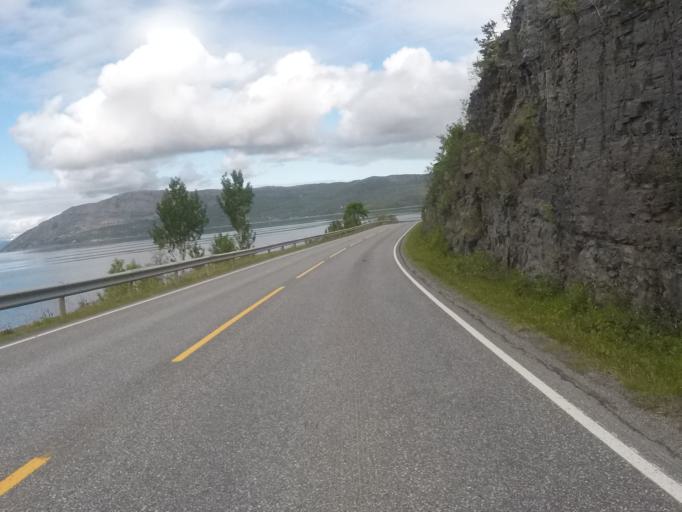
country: NO
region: Finnmark Fylke
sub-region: Alta
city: Alta
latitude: 69.9976
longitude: 23.4796
